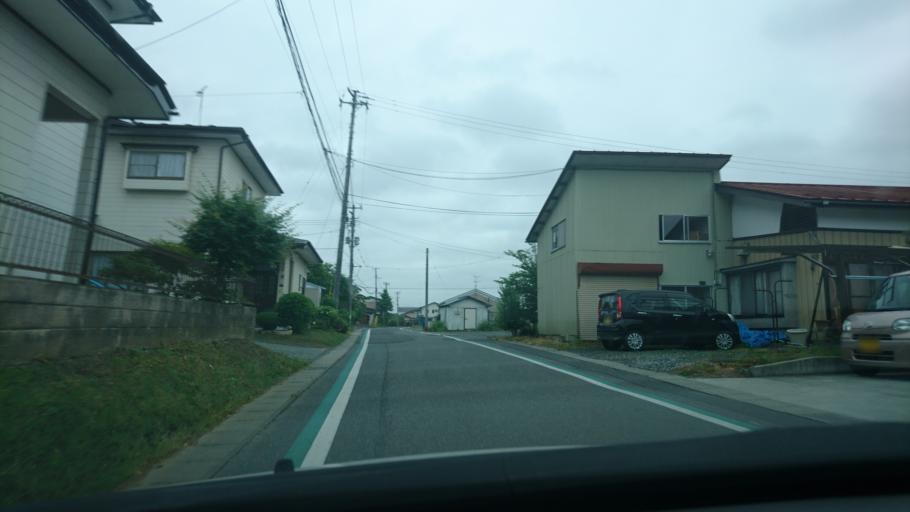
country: JP
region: Iwate
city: Ichinoseki
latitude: 38.9131
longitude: 141.1033
